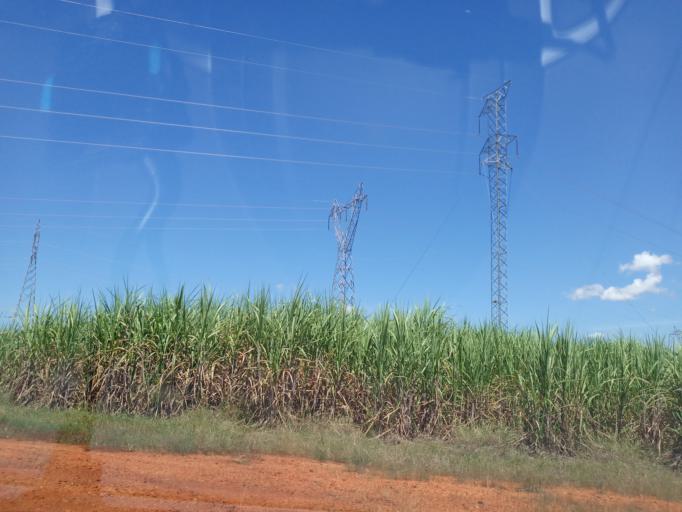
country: BR
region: Goias
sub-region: Itumbiara
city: Itumbiara
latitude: -18.4005
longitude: -49.1211
